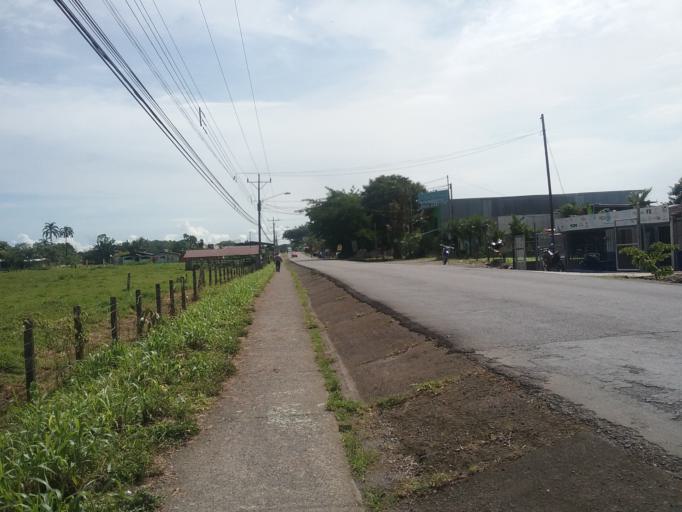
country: CR
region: Limon
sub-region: Canton de Pococi
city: Guapiles
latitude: 10.3204
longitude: -83.9053
